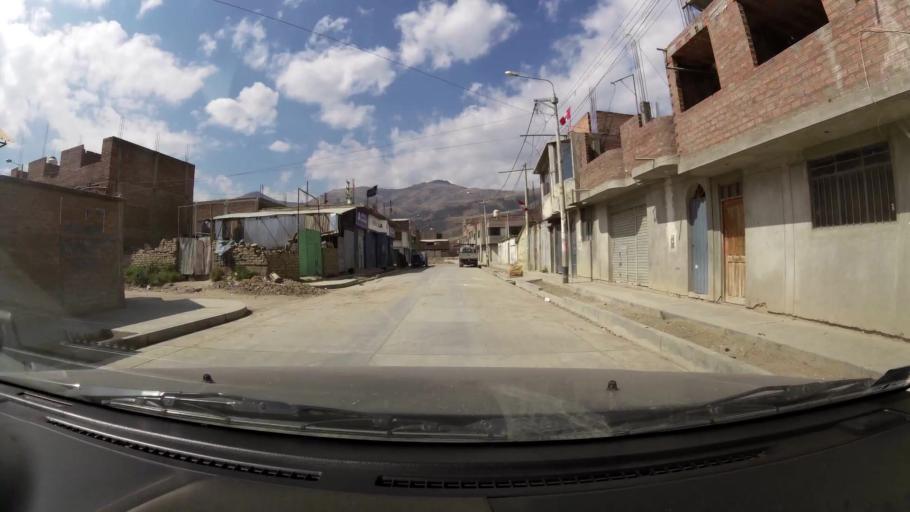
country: PE
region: Junin
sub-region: Provincia de Huancayo
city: Huancayo
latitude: -12.0911
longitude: -75.2017
